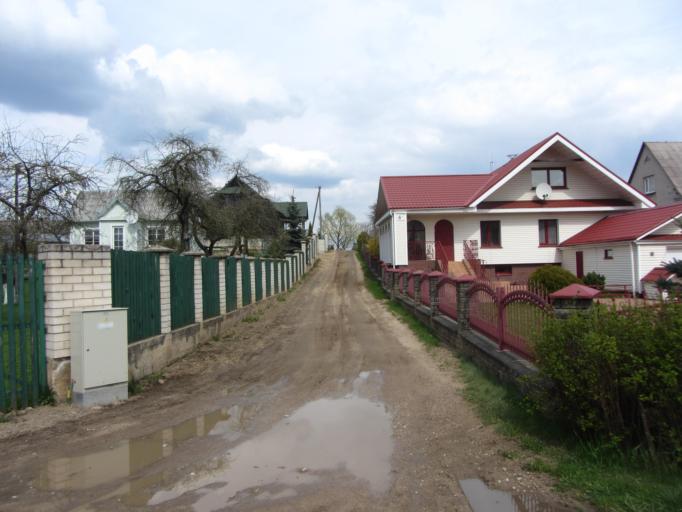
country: LT
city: Lentvaris
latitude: 54.6482
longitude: 25.0626
